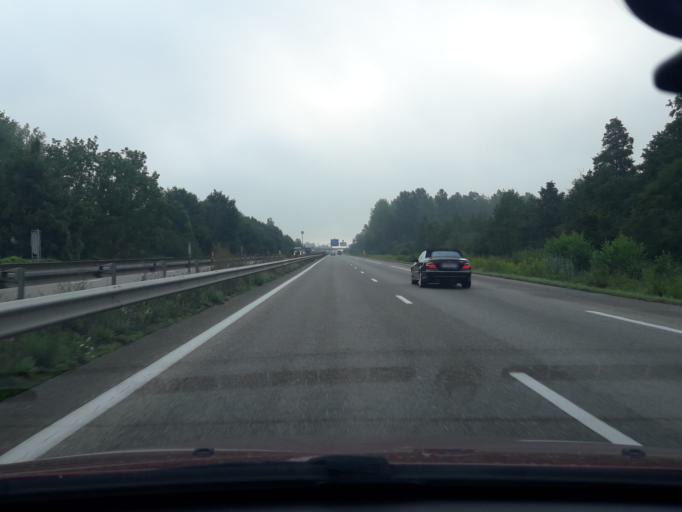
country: FR
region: Alsace
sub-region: Departement du Bas-Rhin
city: Kilstett
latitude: 48.7015
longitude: 7.8460
